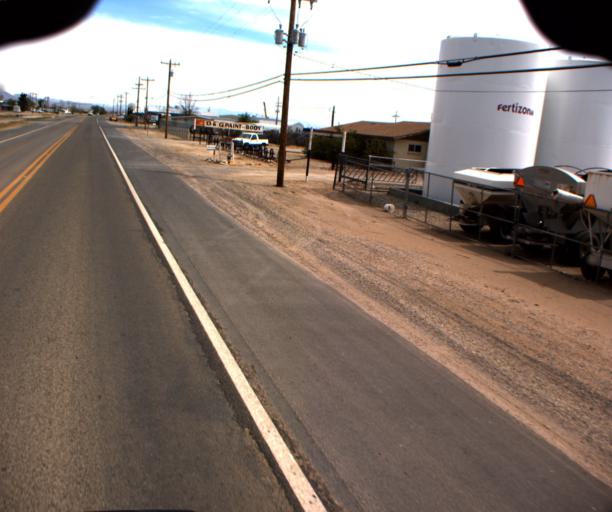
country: US
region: Arizona
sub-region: Cochise County
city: Willcox
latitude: 32.2494
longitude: -109.8260
